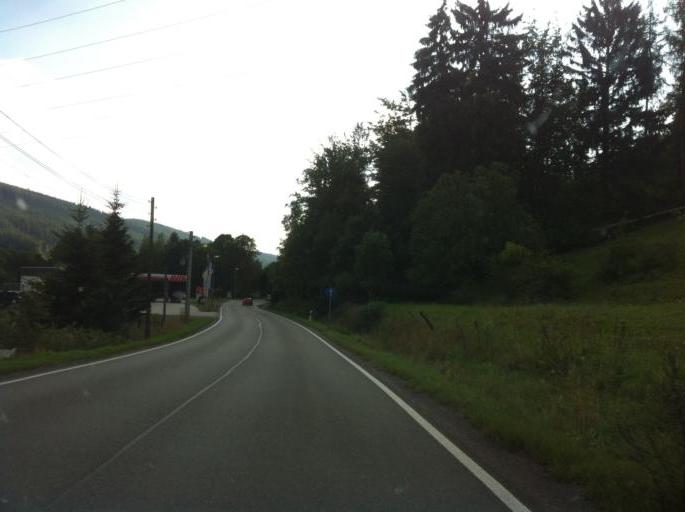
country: DE
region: Thuringia
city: Mohrenbach
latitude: 50.6402
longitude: 11.0023
